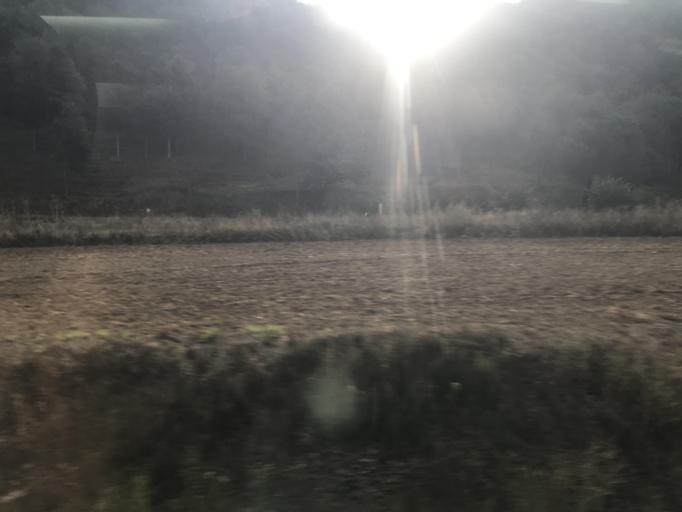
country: ES
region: Castille and Leon
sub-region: Provincia de Burgos
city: Pradanos de Bureba
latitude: 42.5217
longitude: -3.3339
